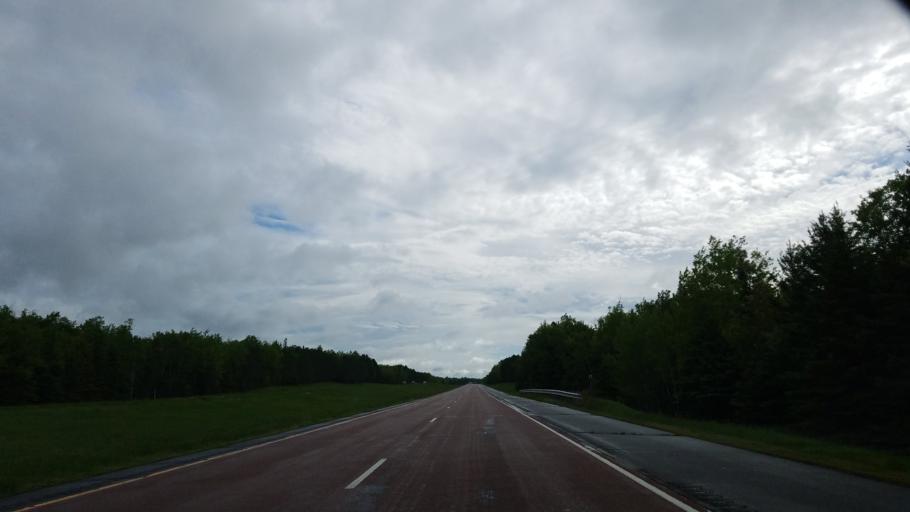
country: US
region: Minnesota
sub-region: Saint Louis County
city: Arnold
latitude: 46.9175
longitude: -91.8713
